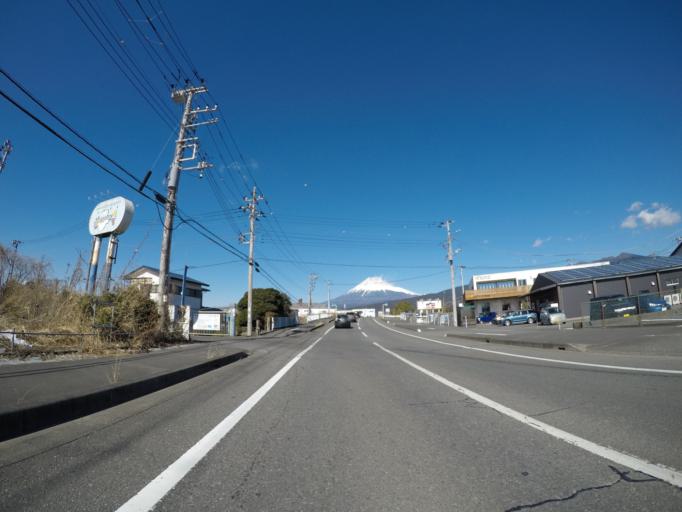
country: JP
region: Shizuoka
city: Fuji
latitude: 35.1422
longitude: 138.7408
